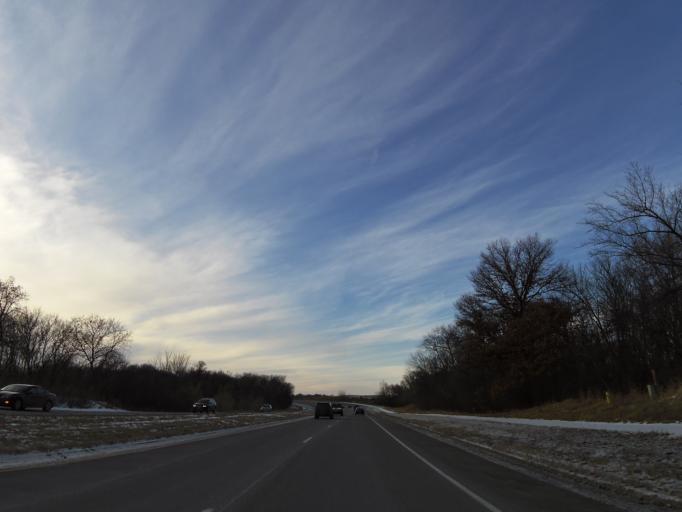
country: US
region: Minnesota
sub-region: Scott County
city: Prior Lake
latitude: 44.6823
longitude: -93.3528
